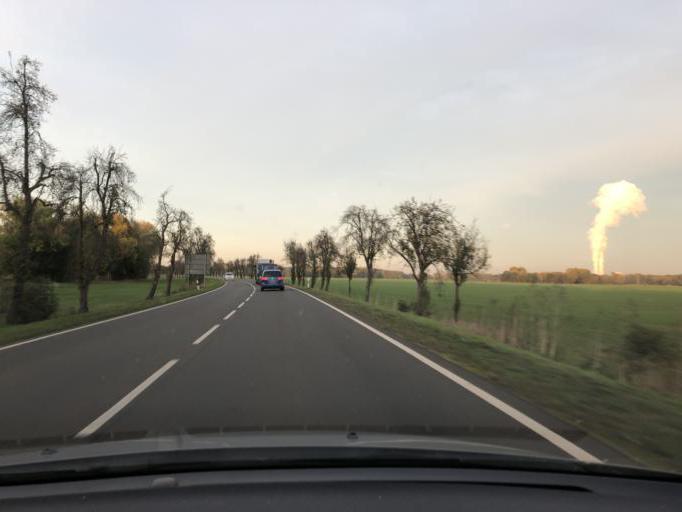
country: DE
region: Saxony
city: Elstertrebnitz
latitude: 51.1476
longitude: 12.2448
